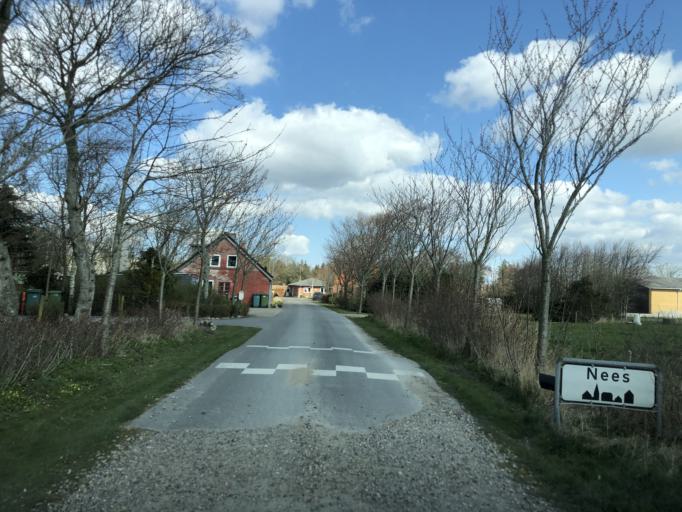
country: DK
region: Central Jutland
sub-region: Holstebro Kommune
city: Ulfborg
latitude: 56.3939
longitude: 8.2146
